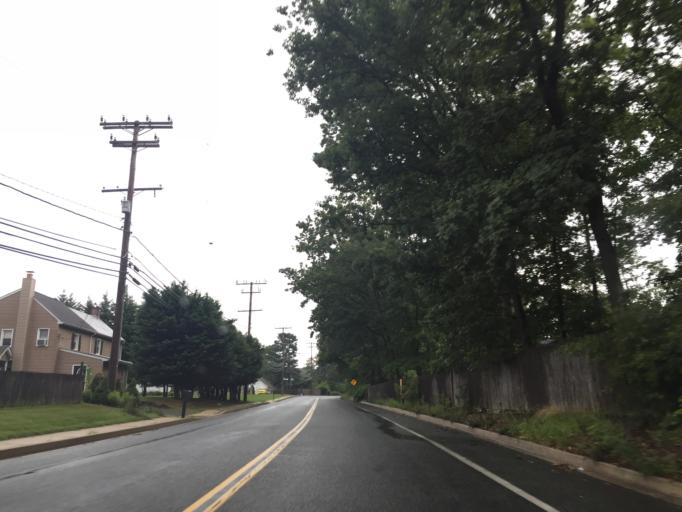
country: US
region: Maryland
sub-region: Harford County
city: Bel Air South
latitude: 39.4750
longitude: -76.3041
